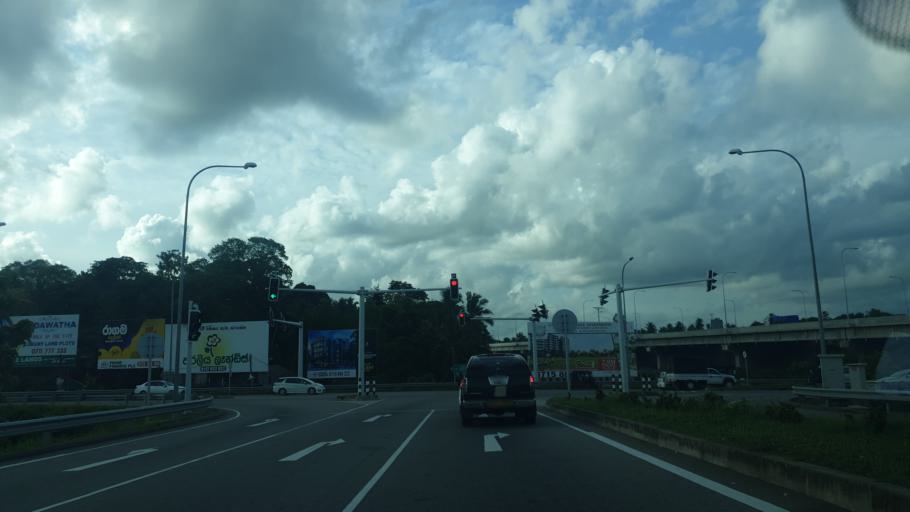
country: LK
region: Western
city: Kelaniya
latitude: 7.0020
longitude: 79.9601
